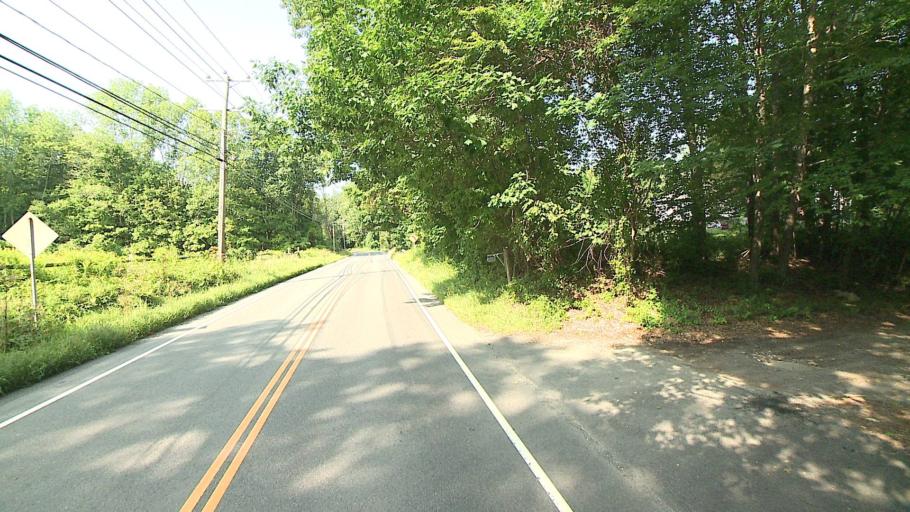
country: US
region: Connecticut
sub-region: Litchfield County
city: Kent
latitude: 41.7695
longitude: -73.4242
